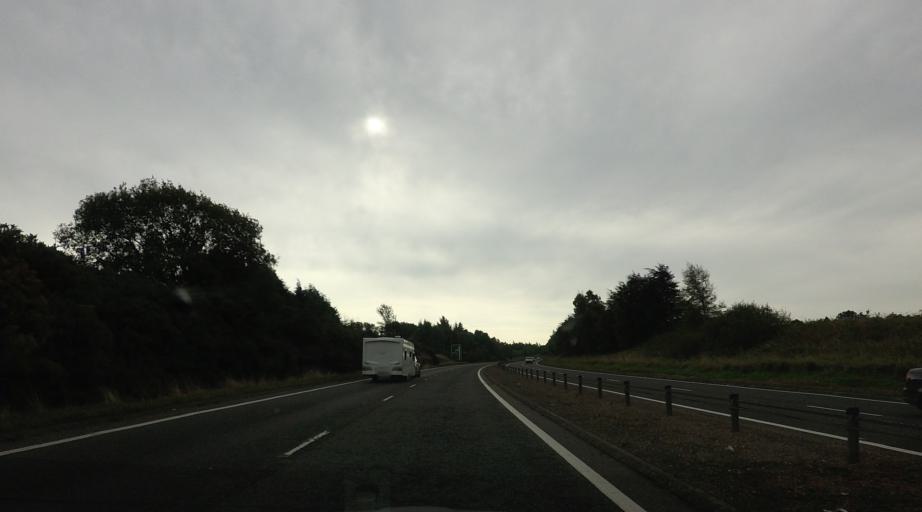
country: GB
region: Scotland
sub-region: Highland
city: Inverness
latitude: 57.4614
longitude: -4.1682
